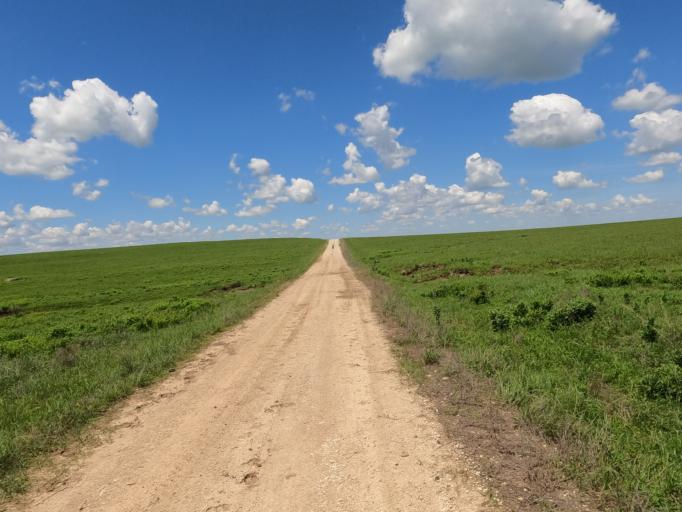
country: US
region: Kansas
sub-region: Marion County
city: Marion
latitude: 38.2419
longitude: -96.7892
